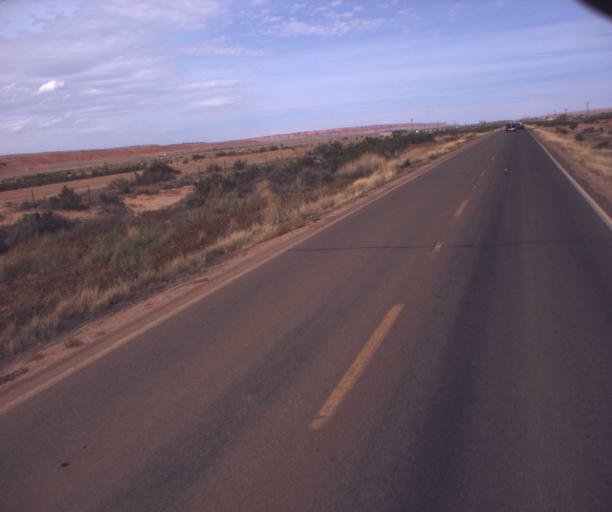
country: US
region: Arizona
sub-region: Apache County
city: Many Farms
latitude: 36.3759
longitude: -109.6123
